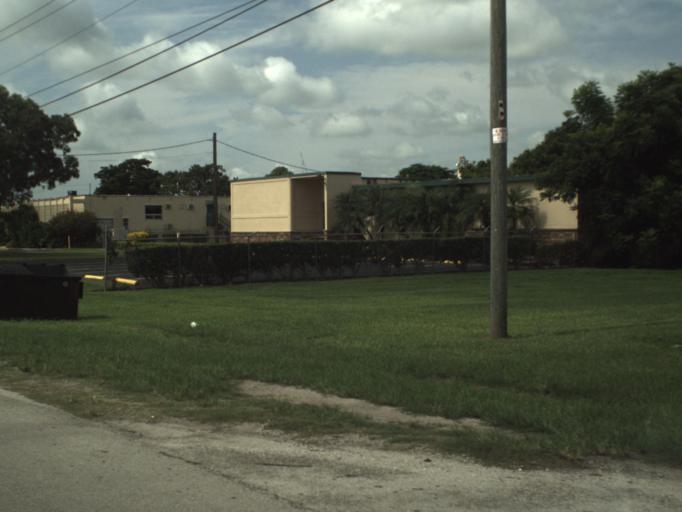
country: US
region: Florida
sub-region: Palm Beach County
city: Belle Glade
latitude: 26.6844
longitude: -80.6840
